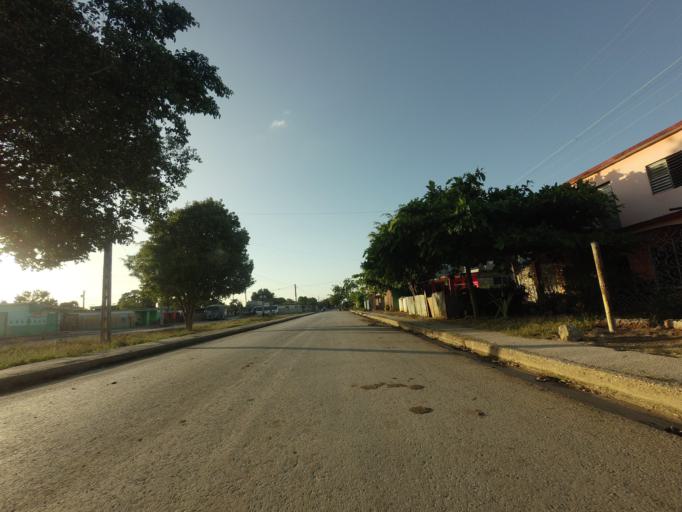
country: CU
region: Ciego de Avila
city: Ciego de Avila
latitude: 21.8285
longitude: -78.7510
